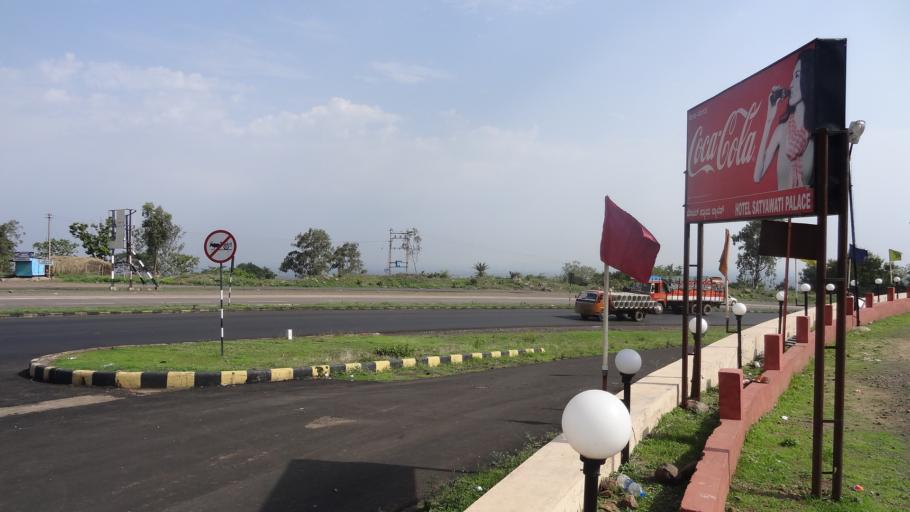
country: IN
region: Maharashtra
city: Nipani
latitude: 16.3485
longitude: 74.3946
